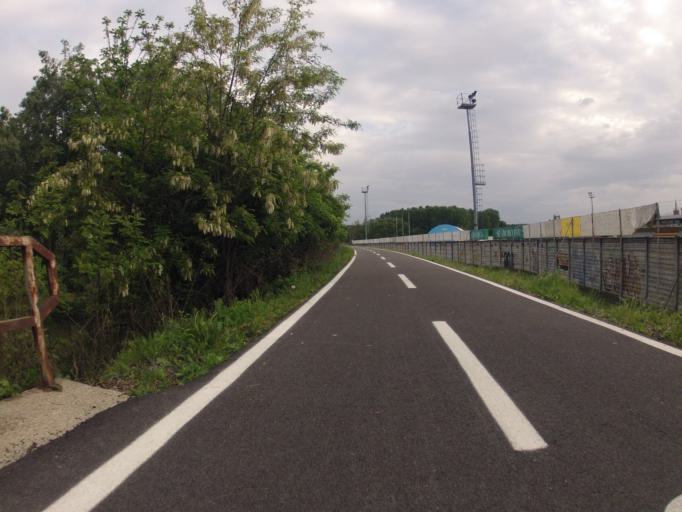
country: IT
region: Piedmont
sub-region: Provincia di Torino
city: Villafranca Piemonte
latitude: 44.7831
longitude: 7.5105
